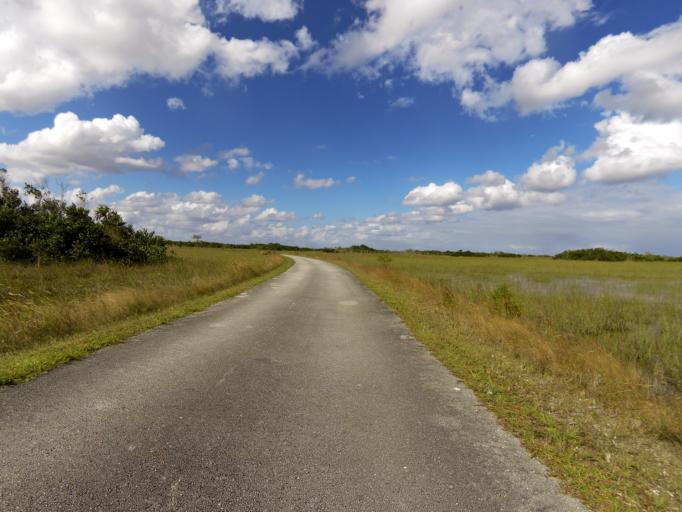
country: US
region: Florida
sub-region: Miami-Dade County
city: The Hammocks
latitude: 25.7156
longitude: -80.7591
